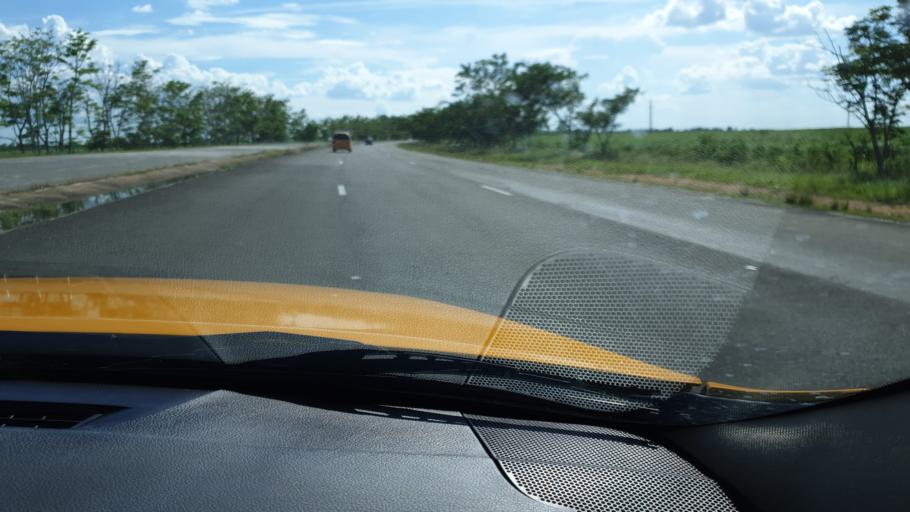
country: CU
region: Cienfuegos
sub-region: Municipio de Aguada de Pasajeros
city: Aguada de Pasajeros
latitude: 22.4031
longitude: -80.8464
